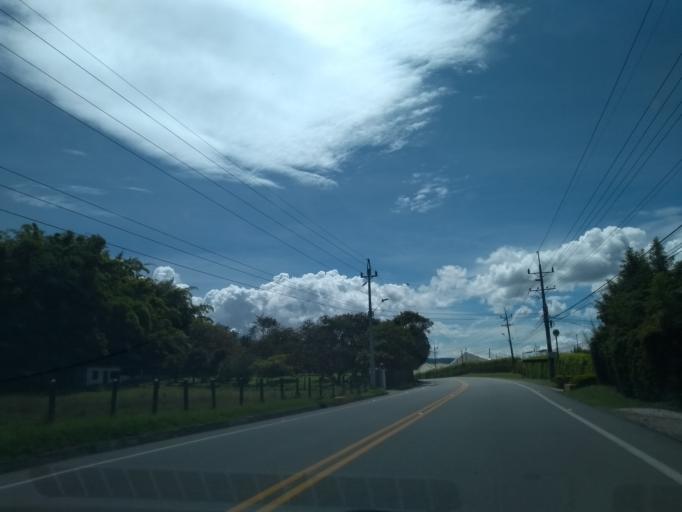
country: CO
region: Antioquia
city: Carmen de Viboral
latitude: 6.0692
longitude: -75.3812
